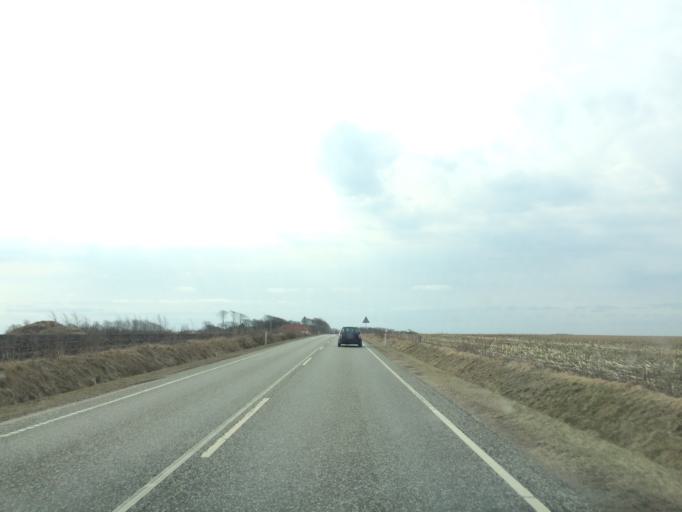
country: DK
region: Central Jutland
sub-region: Ringkobing-Skjern Kommune
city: Skjern
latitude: 56.0258
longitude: 8.5023
